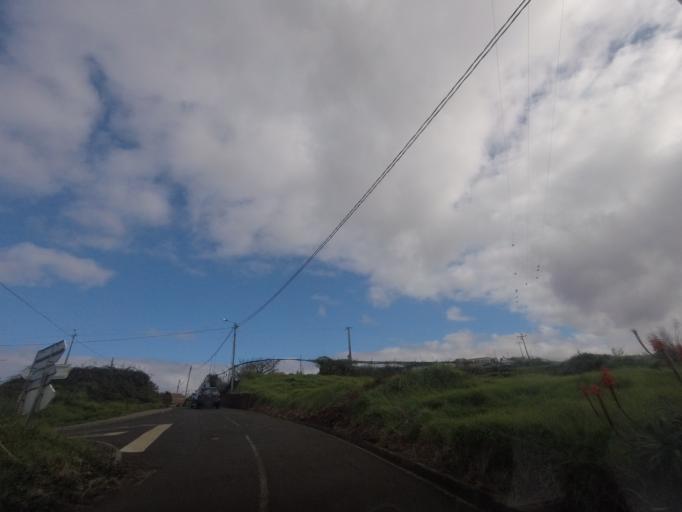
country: PT
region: Madeira
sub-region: Calheta
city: Faja da Ovelha
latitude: 32.8116
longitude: -17.2525
